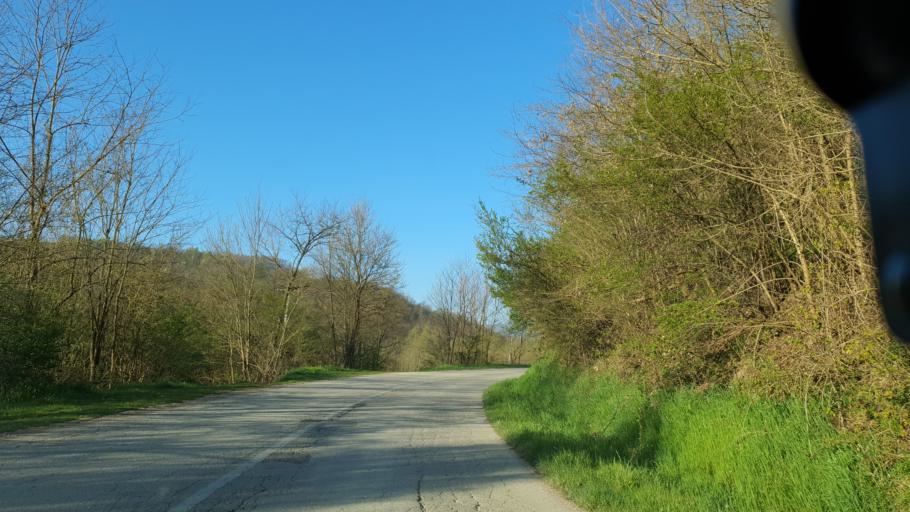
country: RS
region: Central Serbia
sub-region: Kolubarski Okrug
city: Osecina
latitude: 44.3600
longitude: 19.5395
